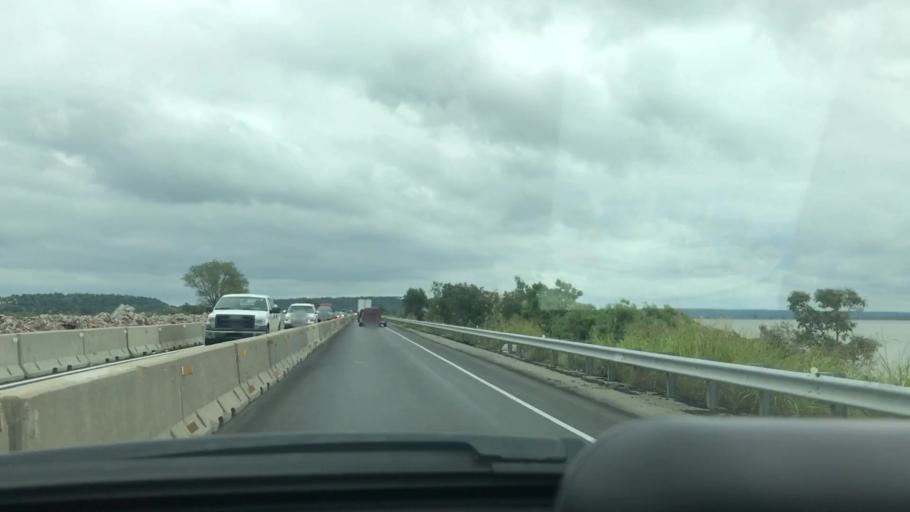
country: US
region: Oklahoma
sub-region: McIntosh County
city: Eufaula
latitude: 35.2292
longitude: -95.5991
